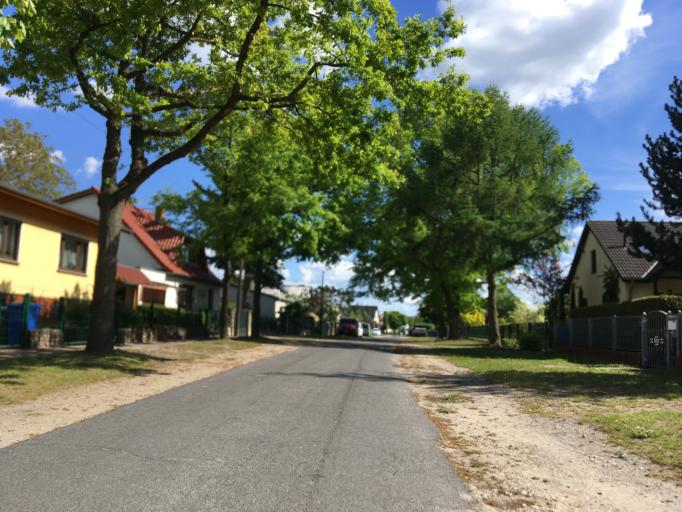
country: DE
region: Brandenburg
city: Bernau bei Berlin
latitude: 52.6783
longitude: 13.5747
